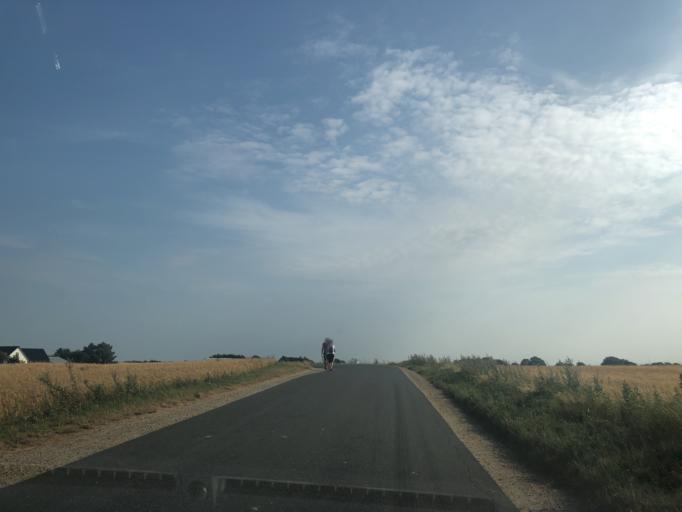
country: DK
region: North Denmark
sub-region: Morso Kommune
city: Nykobing Mors
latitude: 56.8229
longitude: 9.0194
